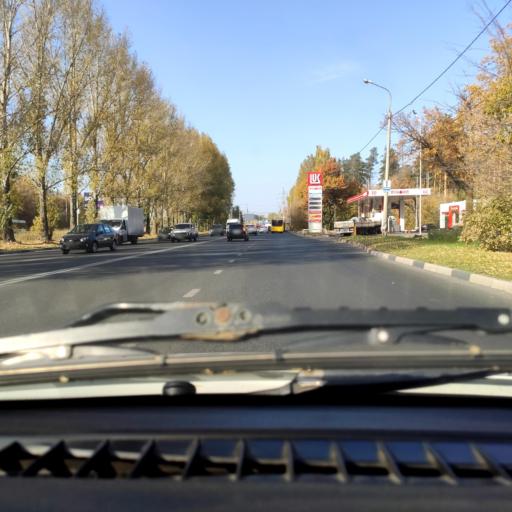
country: RU
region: Samara
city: Zhigulevsk
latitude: 53.5082
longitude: 49.4645
